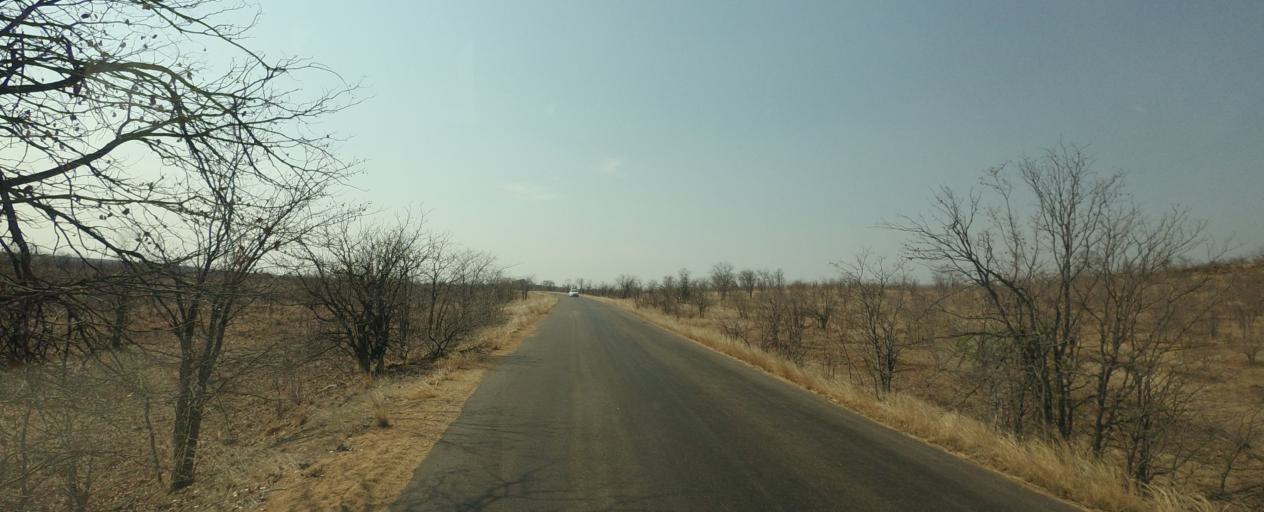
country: ZA
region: Limpopo
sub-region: Mopani District Municipality
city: Phalaborwa
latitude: -23.9681
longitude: 31.6284
